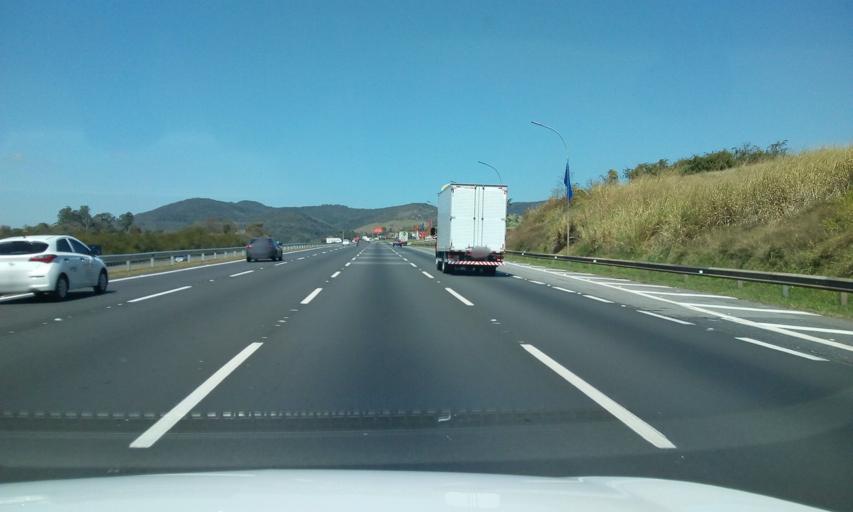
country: BR
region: Sao Paulo
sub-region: Jundiai
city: Jundiai
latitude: -23.2010
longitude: -46.9284
